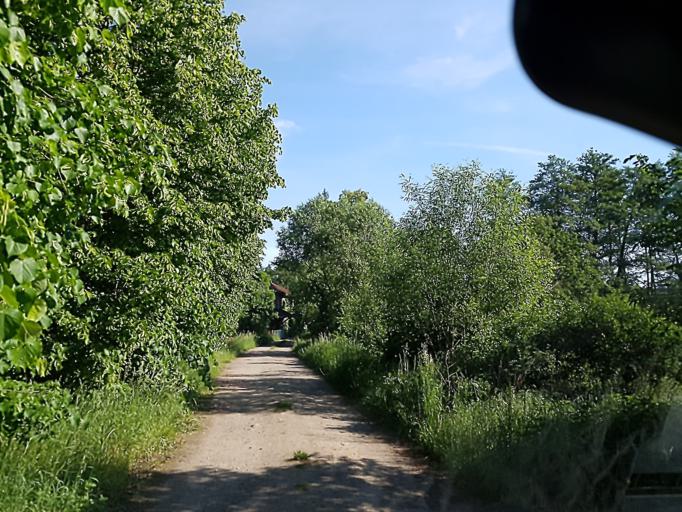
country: DE
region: Saxony-Anhalt
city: Klieken
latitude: 51.9599
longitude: 12.3375
